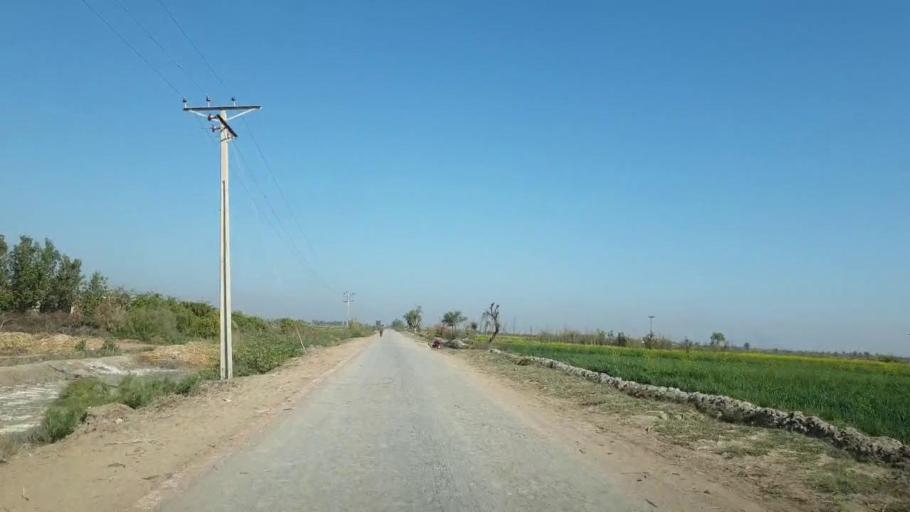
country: PK
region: Sindh
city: Mirpur Khas
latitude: 25.5975
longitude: 69.0451
